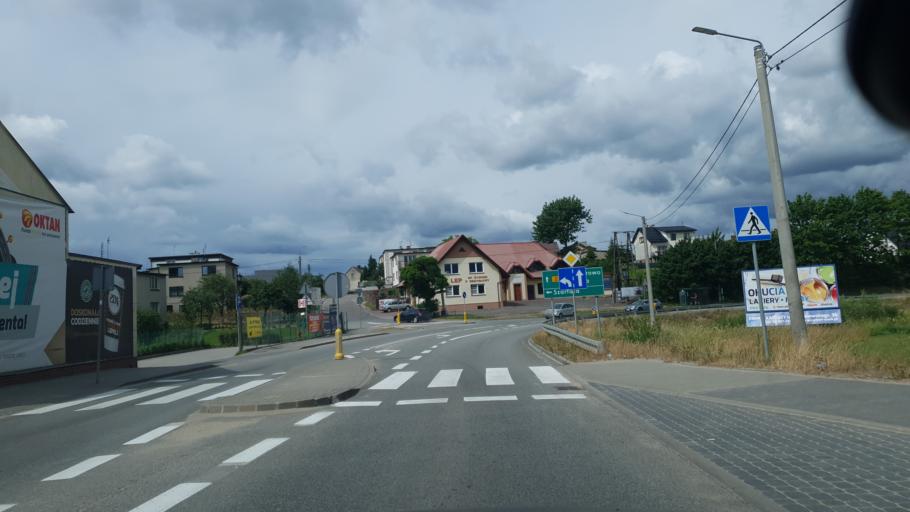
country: PL
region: Pomeranian Voivodeship
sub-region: Powiat kartuski
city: Kartuzy
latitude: 54.3520
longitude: 18.2180
